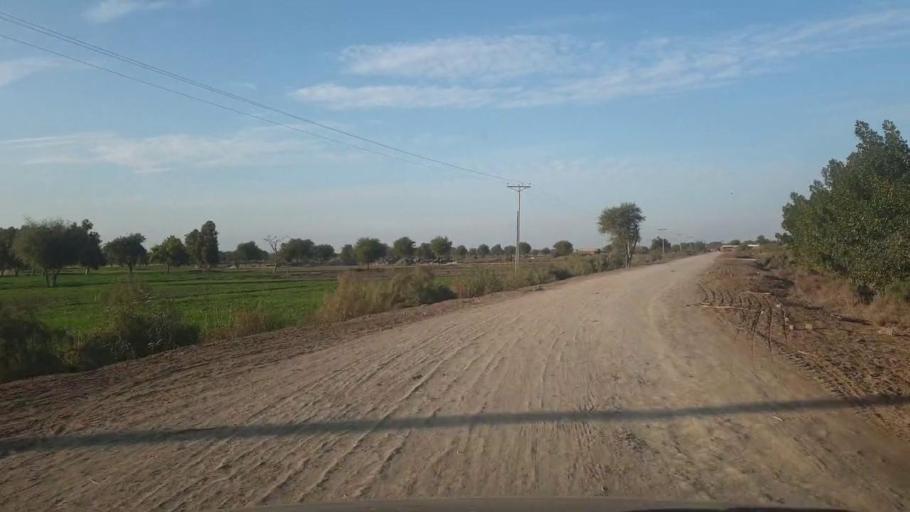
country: PK
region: Sindh
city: Sinjhoro
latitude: 26.0328
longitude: 68.8352
